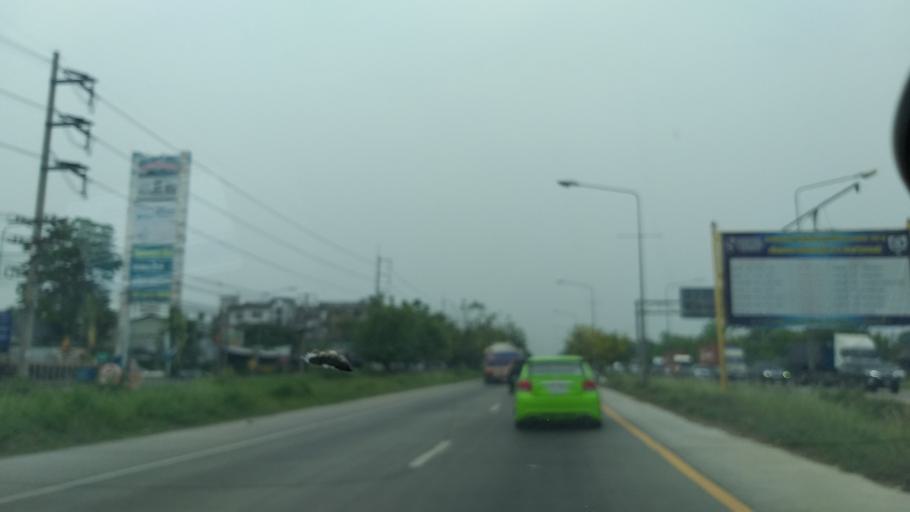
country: TH
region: Chon Buri
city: Ko Chan
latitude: 13.3880
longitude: 101.2791
